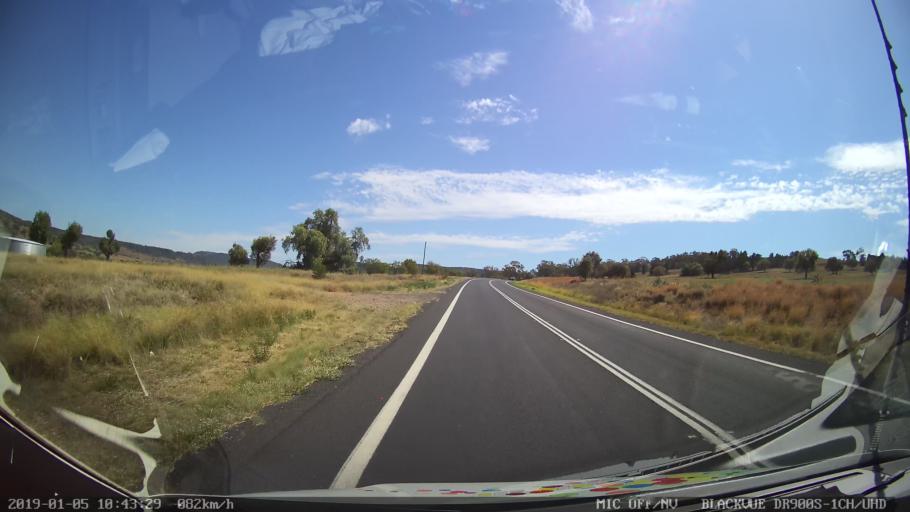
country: AU
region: New South Wales
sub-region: Warrumbungle Shire
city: Coonabarabran
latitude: -31.4642
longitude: 148.9883
